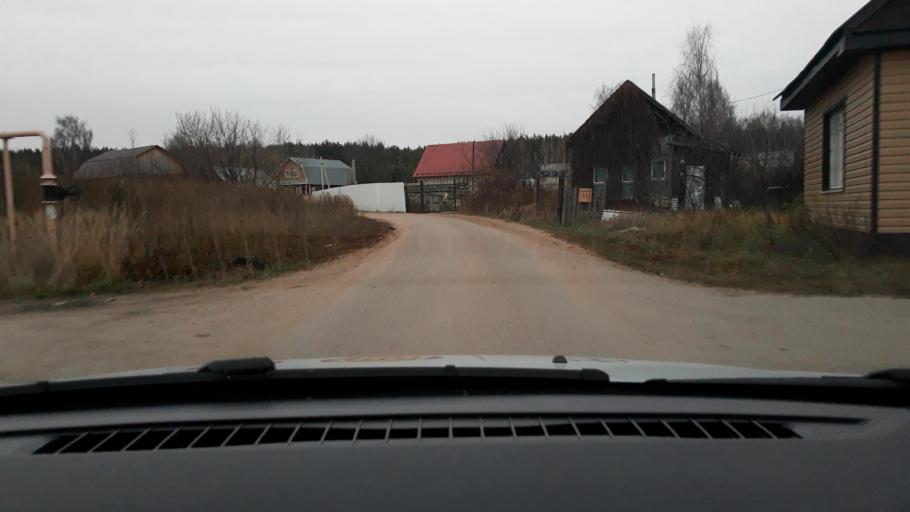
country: RU
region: Nizjnij Novgorod
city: Neklyudovo
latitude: 56.4201
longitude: 44.0211
